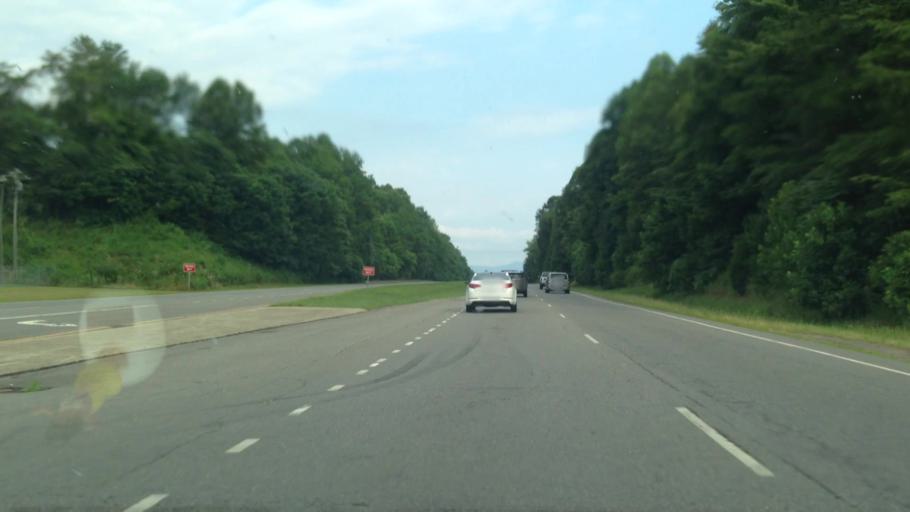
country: US
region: North Carolina
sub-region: Surry County
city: Mount Airy
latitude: 36.4733
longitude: -80.5792
